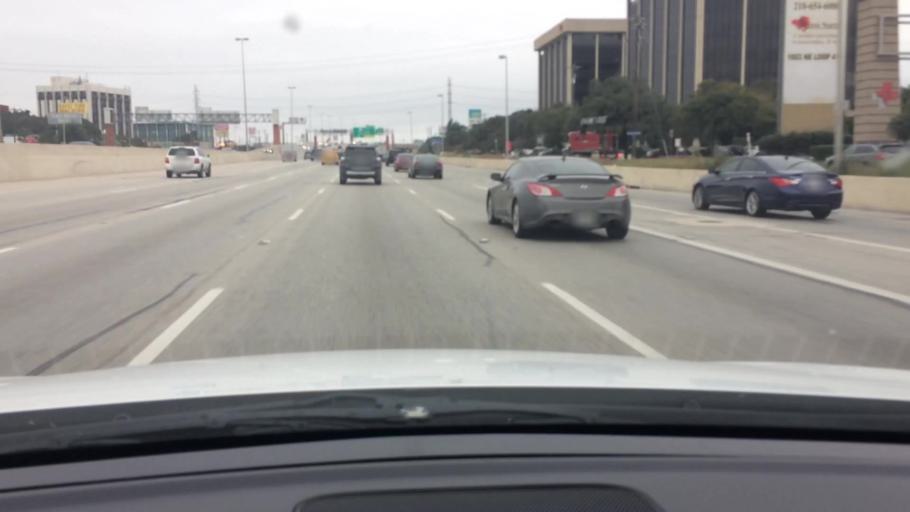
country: US
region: Texas
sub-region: Bexar County
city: Alamo Heights
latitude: 29.5164
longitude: -98.4582
